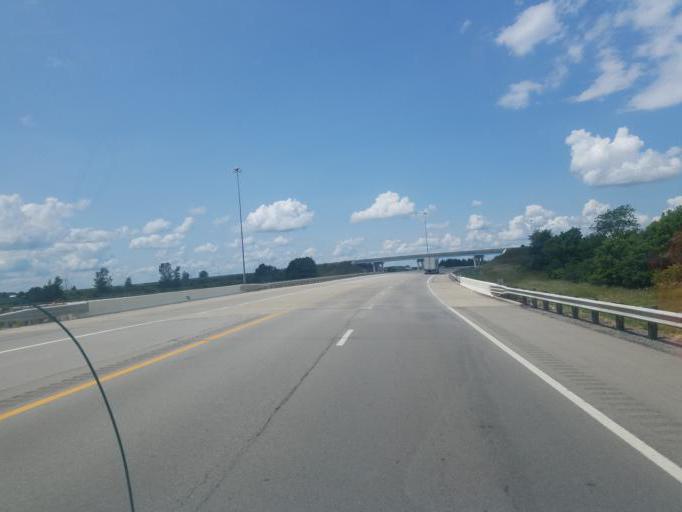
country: US
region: Ohio
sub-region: Wyandot County
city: Upper Sandusky
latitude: 40.8602
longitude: -83.3201
